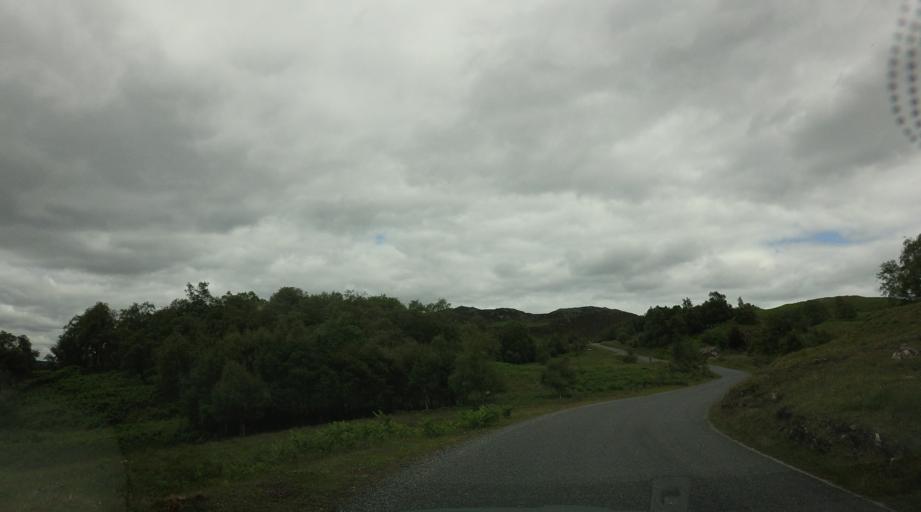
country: GB
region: Scotland
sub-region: Perth and Kinross
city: Aberfeldy
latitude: 56.6908
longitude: -4.1018
